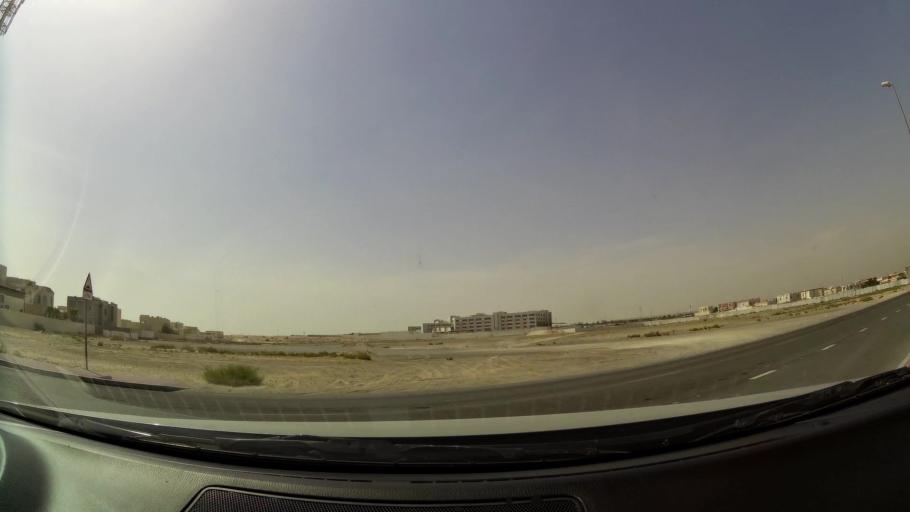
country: AE
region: Ash Shariqah
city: Sharjah
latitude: 25.1980
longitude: 55.4235
